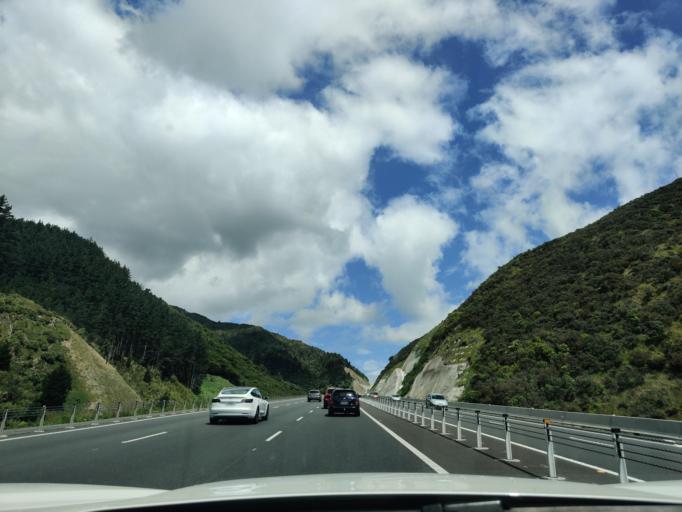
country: NZ
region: Wellington
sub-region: Kapiti Coast District
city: Paraparaumu
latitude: -40.9989
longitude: 174.9642
